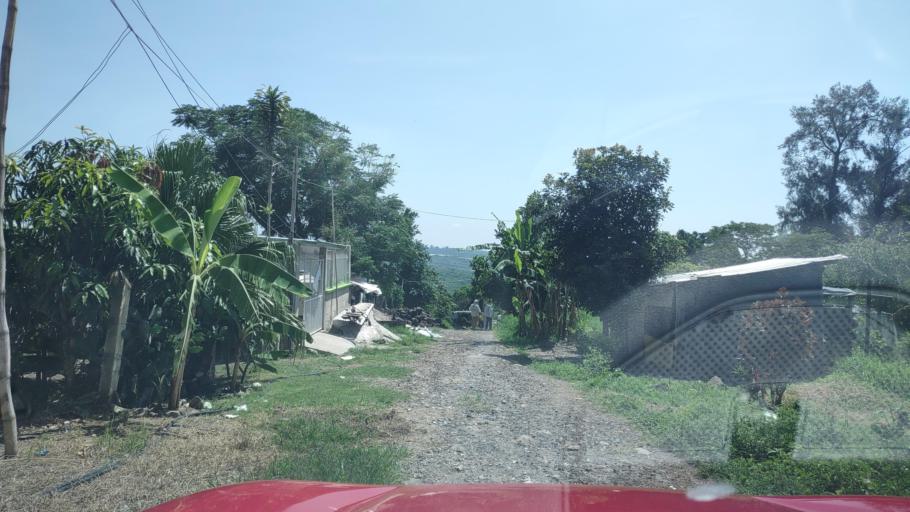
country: MX
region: Veracruz
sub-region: Emiliano Zapata
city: Dos Rios
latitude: 19.4905
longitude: -96.8160
